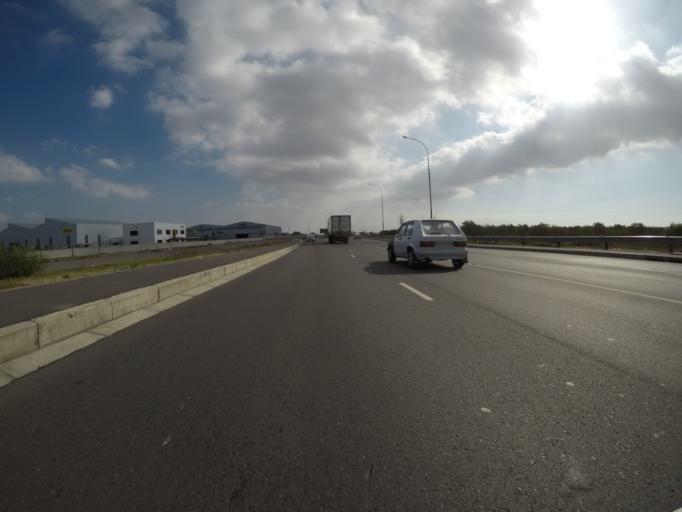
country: ZA
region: Western Cape
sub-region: City of Cape Town
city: Kraaifontein
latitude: -33.9544
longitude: 18.6905
